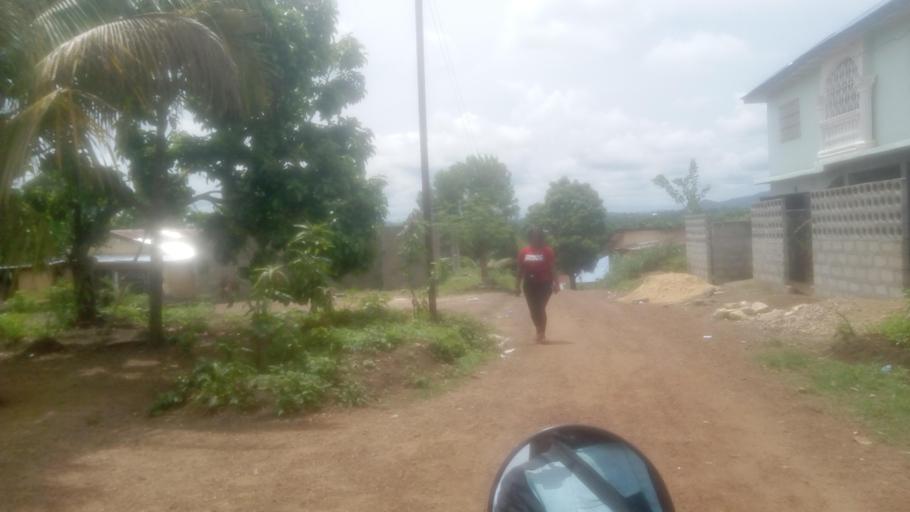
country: SL
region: Southern Province
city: Bo
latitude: 7.9557
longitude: -11.7136
